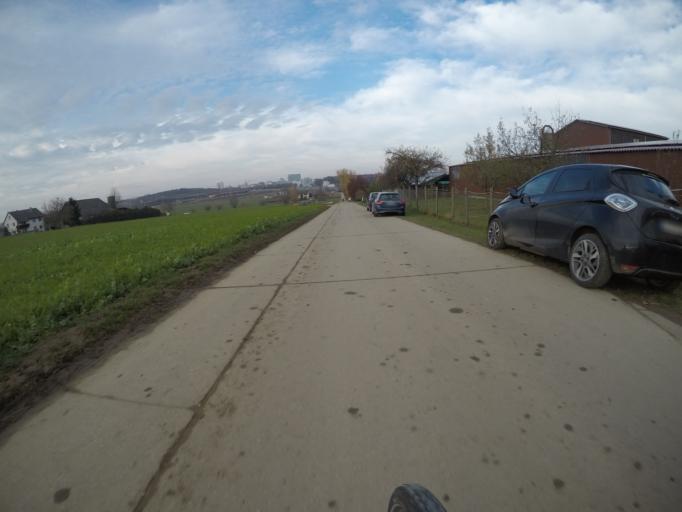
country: DE
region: Baden-Wuerttemberg
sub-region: Regierungsbezirk Stuttgart
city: Leinfelden-Echterdingen
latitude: 48.6988
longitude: 9.1736
